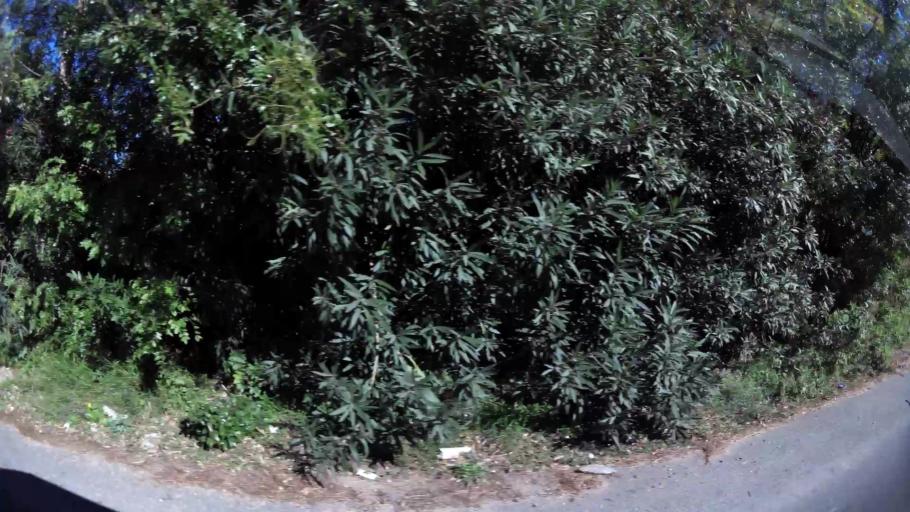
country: GR
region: Attica
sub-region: Nomarchia Anatolikis Attikis
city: Paiania
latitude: 37.9640
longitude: 23.8547
